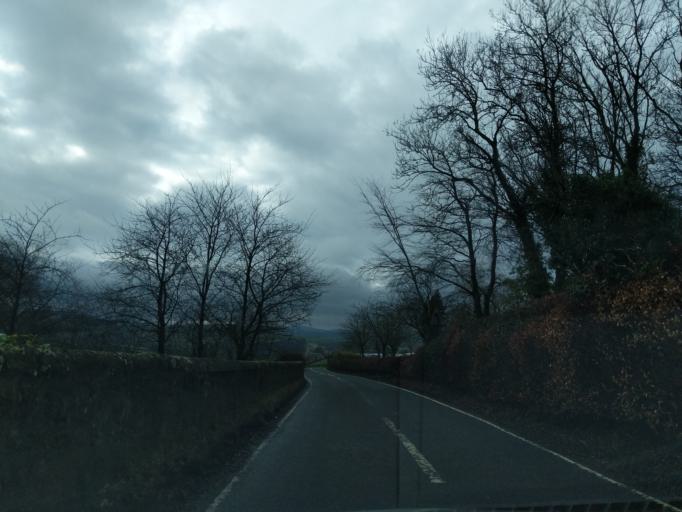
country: GB
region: Scotland
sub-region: South Lanarkshire
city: Carluke
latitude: 55.7087
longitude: -3.8463
